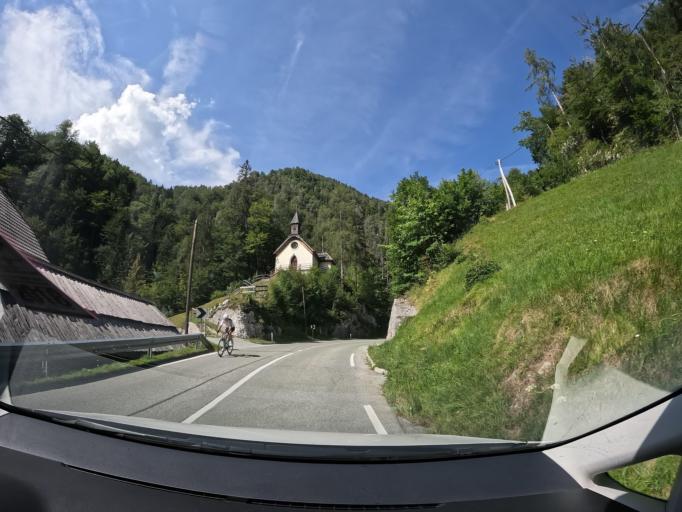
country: SI
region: Trzic
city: Trzic
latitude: 46.4126
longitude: 14.2976
